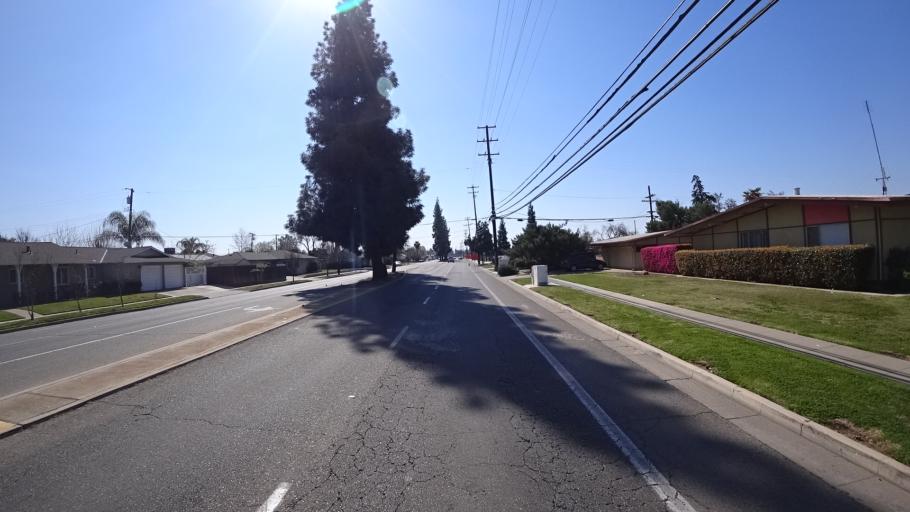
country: US
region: California
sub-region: Fresno County
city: Fresno
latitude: 36.7674
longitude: -119.8268
